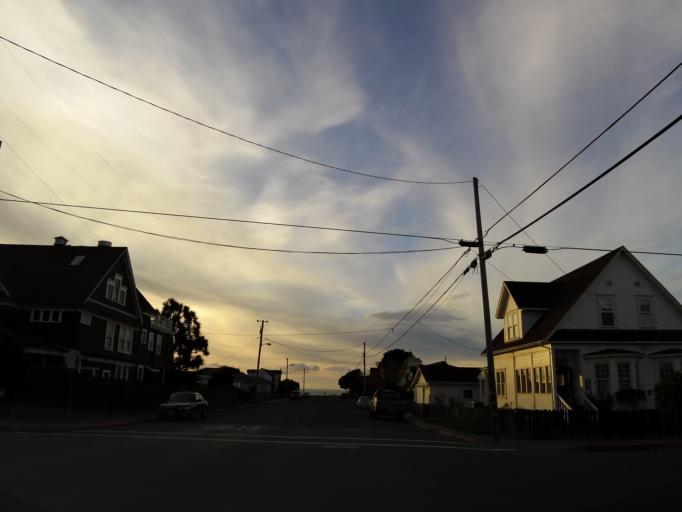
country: US
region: California
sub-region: Mendocino County
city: Fort Bragg
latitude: 39.4481
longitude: -123.8071
